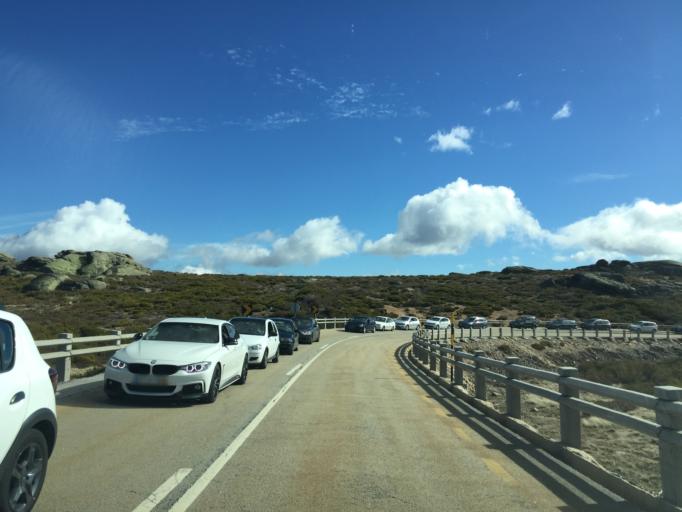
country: PT
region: Castelo Branco
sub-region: Covilha
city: Covilha
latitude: 40.3169
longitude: -7.5645
